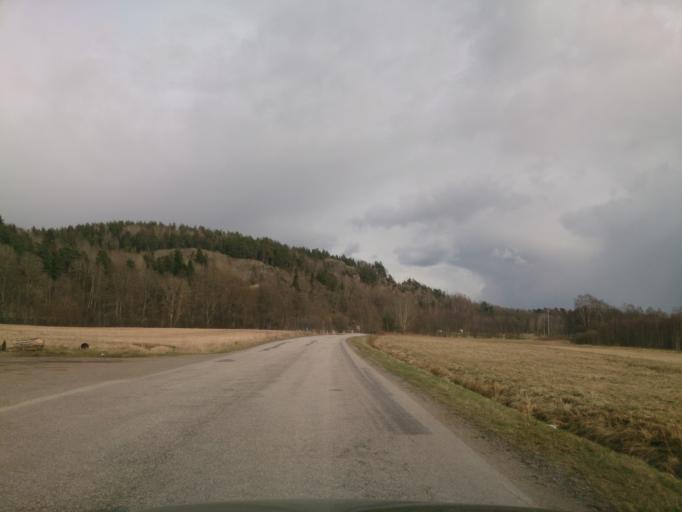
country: SE
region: OEstergoetland
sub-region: Norrkopings Kommun
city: Jursla
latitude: 58.6730
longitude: 16.1504
